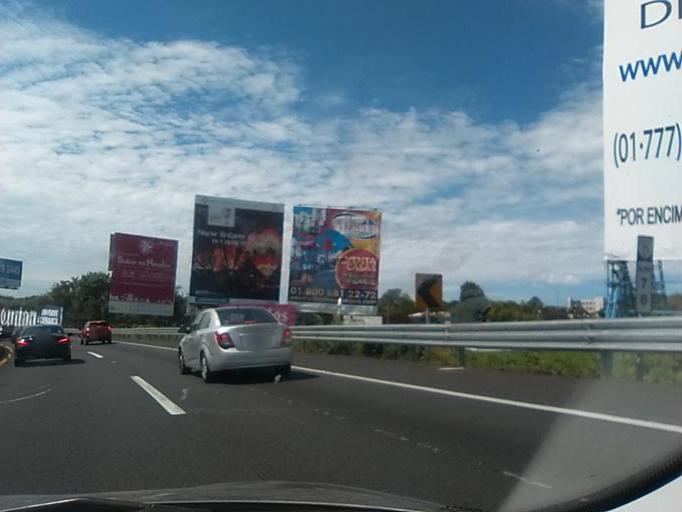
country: MX
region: Morelos
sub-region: Cuernavaca
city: Fraccionamiento Lomas de Ahuatlan
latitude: 18.9805
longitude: -99.2309
